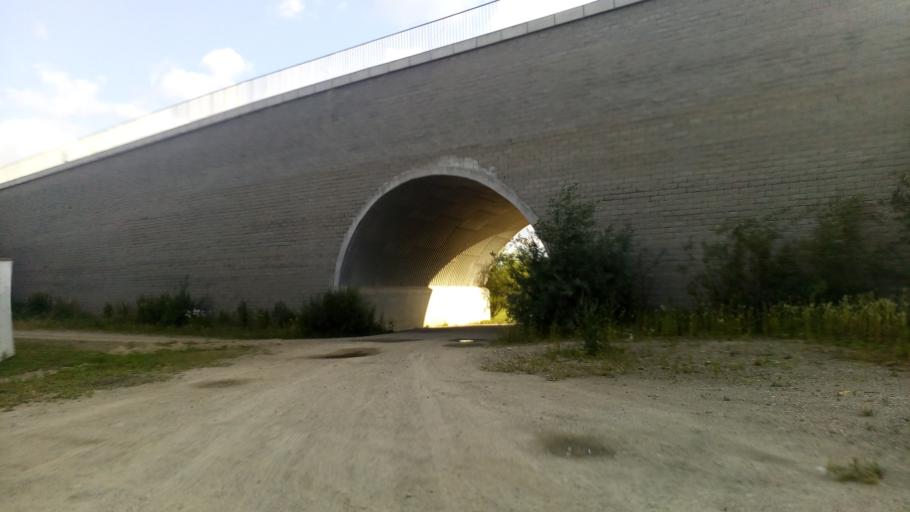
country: PL
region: Lesser Poland Voivodeship
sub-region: Powiat nowosadecki
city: Stary Sacz
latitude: 49.5732
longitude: 20.6466
